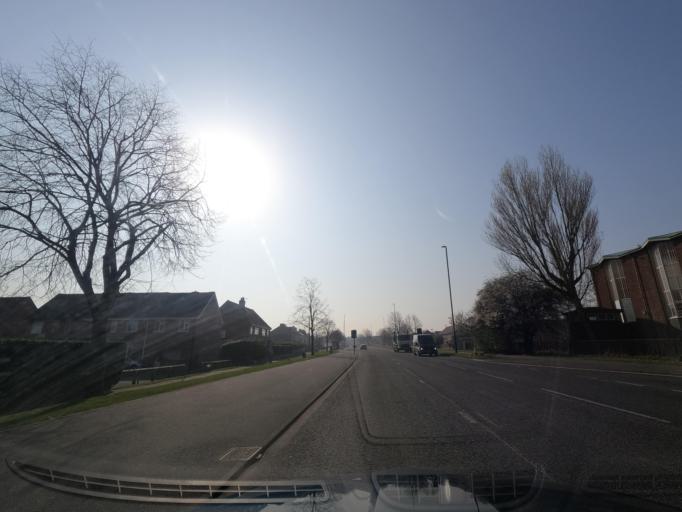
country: GB
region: England
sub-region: Newcastle upon Tyne
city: Gosforth
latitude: 55.0158
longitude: -1.5838
